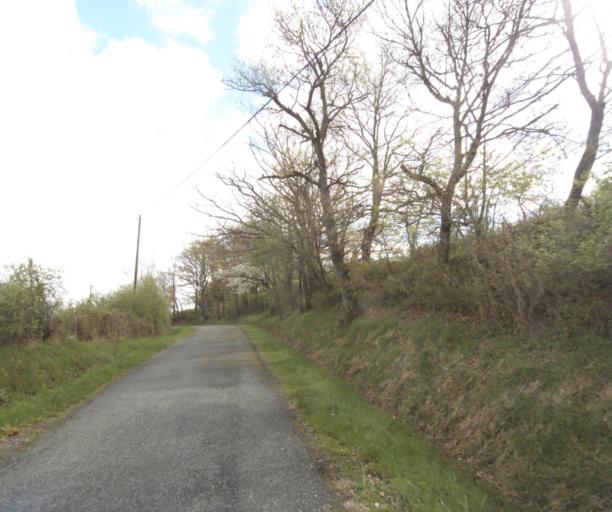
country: FR
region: Midi-Pyrenees
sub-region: Departement de l'Ariege
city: Saverdun
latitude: 43.2273
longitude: 1.5237
